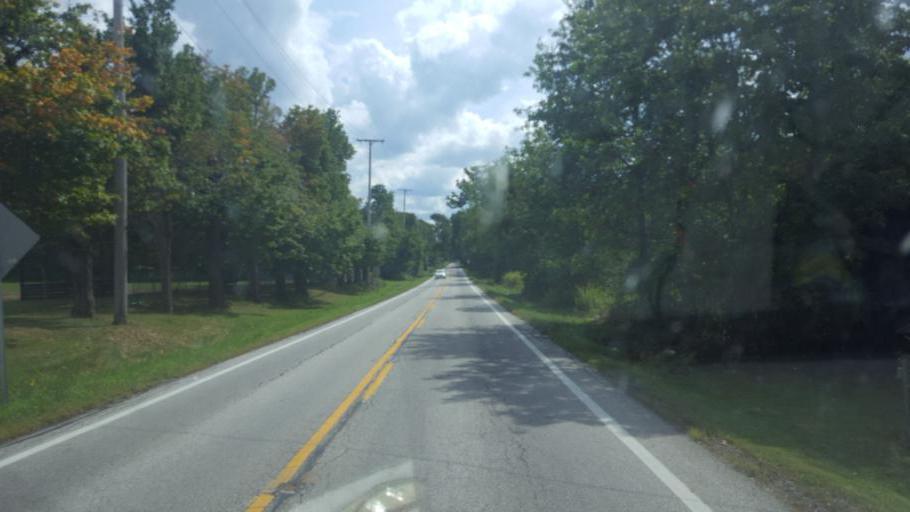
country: US
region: Ohio
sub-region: Portage County
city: Hiram
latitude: 41.3854
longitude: -81.1431
